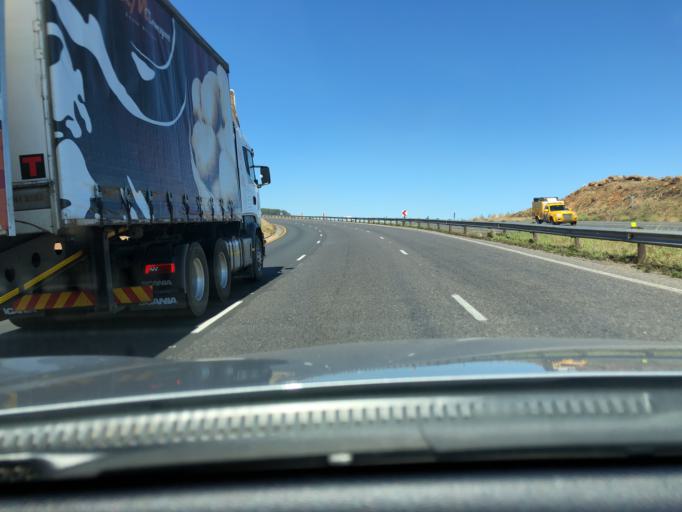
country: ZA
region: KwaZulu-Natal
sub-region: uMgungundlovu District Municipality
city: Howick
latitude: -29.4346
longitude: 30.1716
